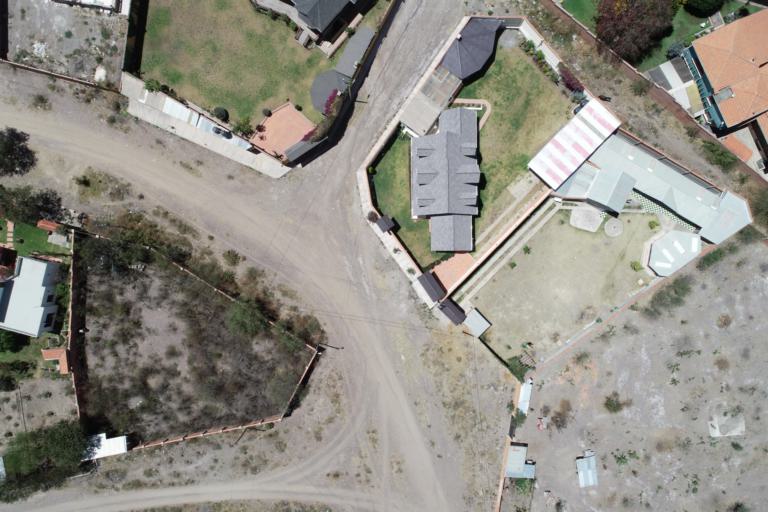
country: BO
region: La Paz
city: La Paz
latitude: -16.6428
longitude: -68.0422
